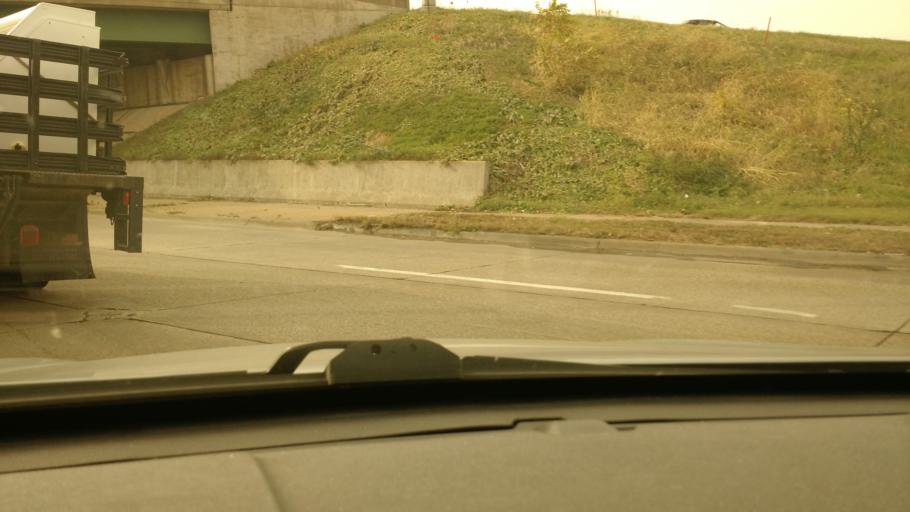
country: US
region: Iowa
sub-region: Scott County
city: Bettendorf
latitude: 41.5414
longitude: -90.5174
